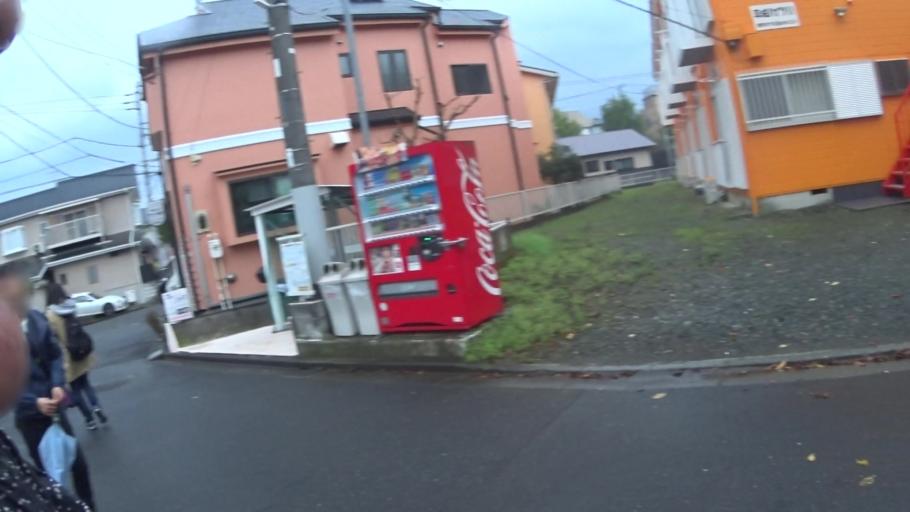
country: JP
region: Kanagawa
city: Hadano
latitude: 35.3670
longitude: 139.2229
